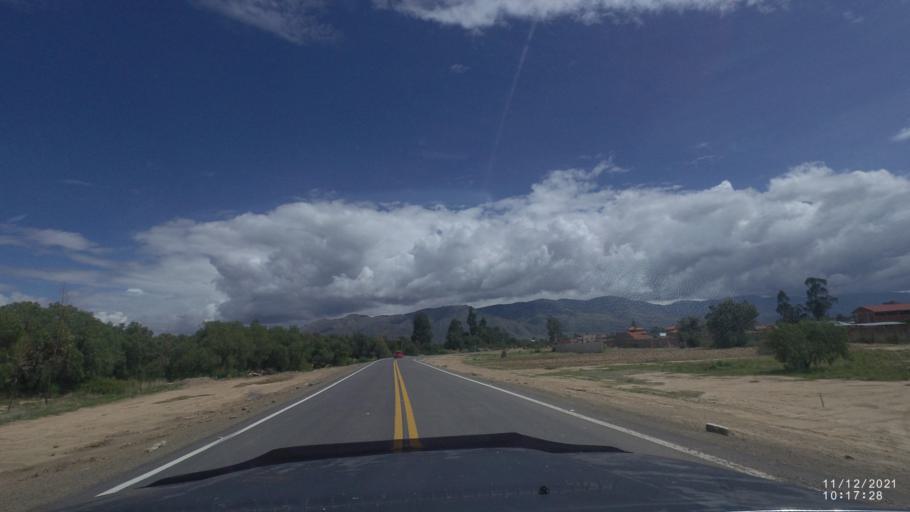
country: BO
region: Cochabamba
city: Tarata
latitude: -17.5866
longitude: -66.0197
